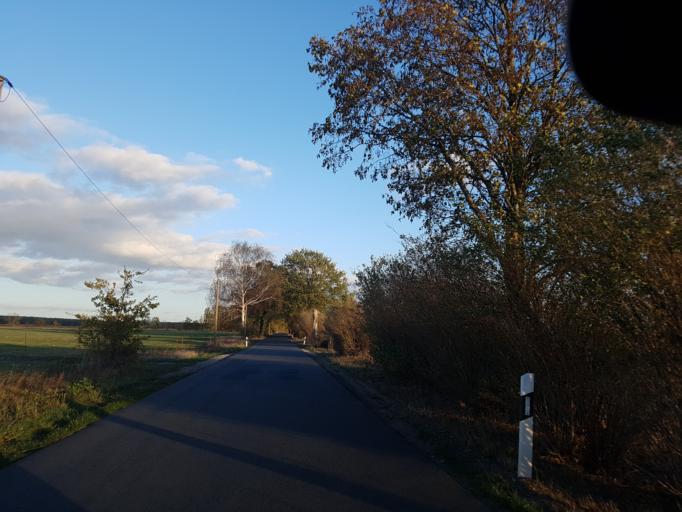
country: DE
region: Brandenburg
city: Beelitz
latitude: 52.1919
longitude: 12.9173
